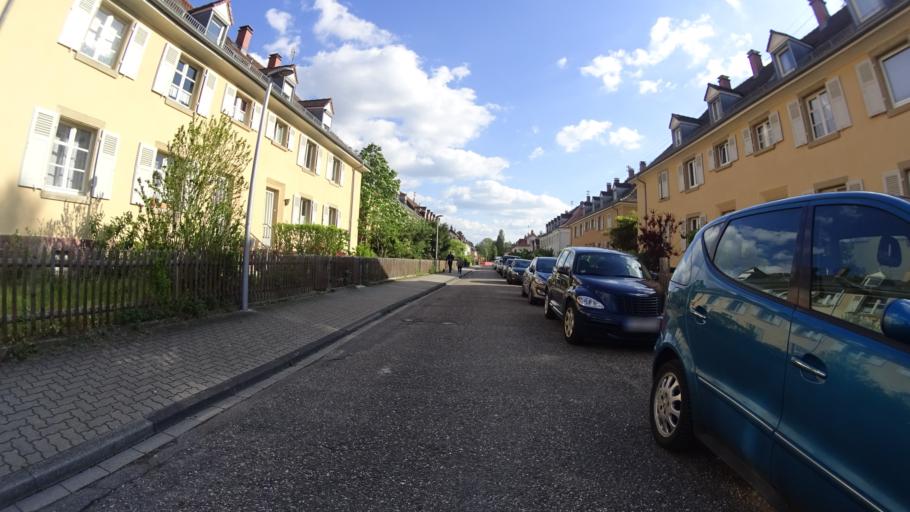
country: DE
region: Baden-Wuerttemberg
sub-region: Karlsruhe Region
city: Karlsruhe
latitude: 49.0211
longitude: 8.3820
